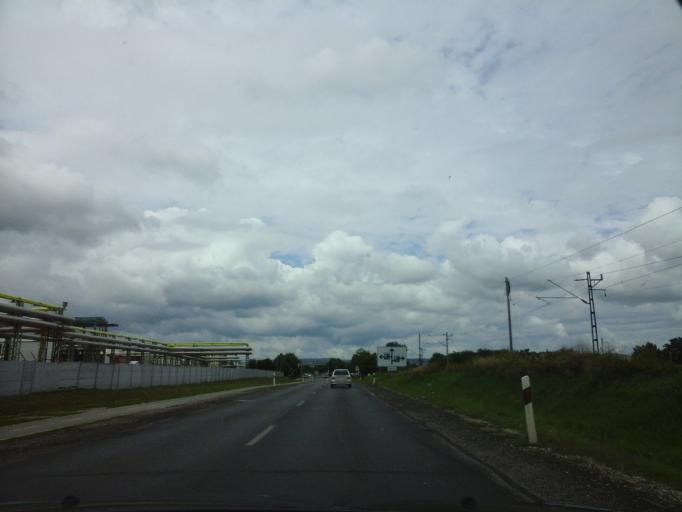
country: HU
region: Borsod-Abauj-Zemplen
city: Mucsony
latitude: 48.2442
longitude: 20.6634
